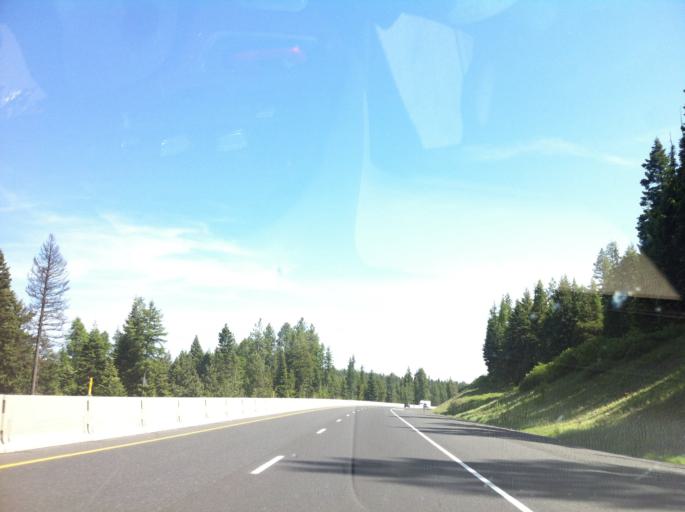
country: US
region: Oregon
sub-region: Union County
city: La Grande
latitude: 45.4752
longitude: -118.3974
